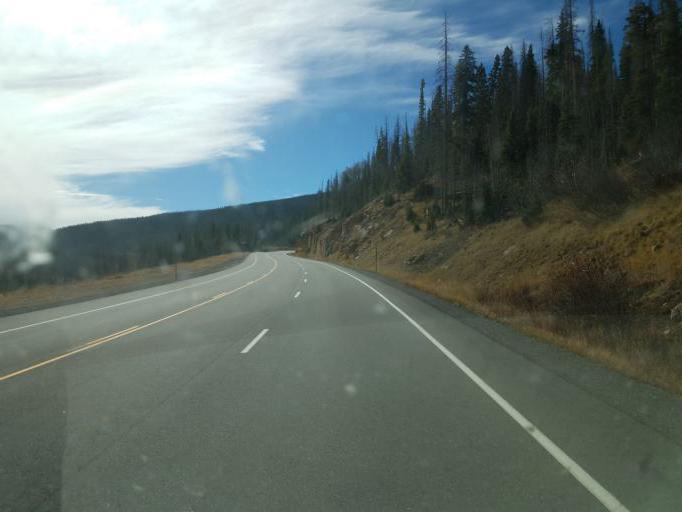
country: US
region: Colorado
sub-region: Archuleta County
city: Pagosa Springs
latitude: 37.5154
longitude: -106.7727
